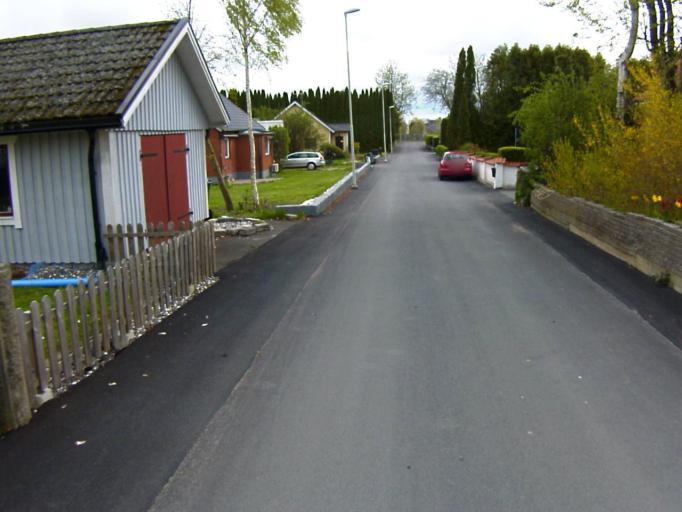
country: SE
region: Skane
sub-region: Kristianstads Kommun
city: Kristianstad
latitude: 56.0522
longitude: 14.1863
